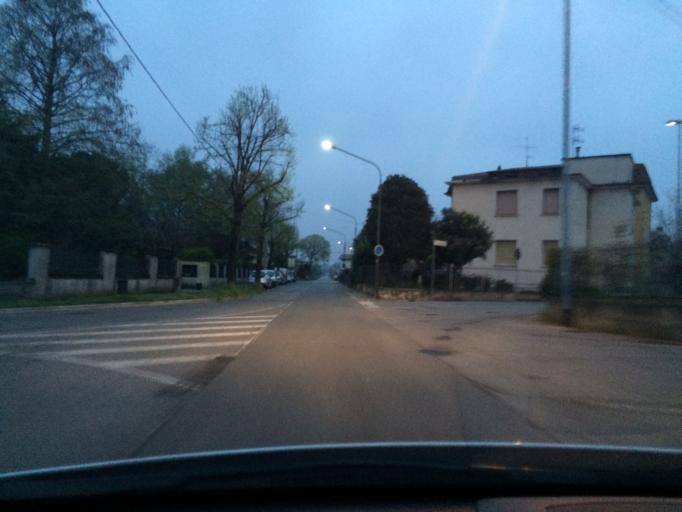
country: IT
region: Lombardy
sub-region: Provincia di Brescia
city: Flero
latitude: 45.4872
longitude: 10.1770
